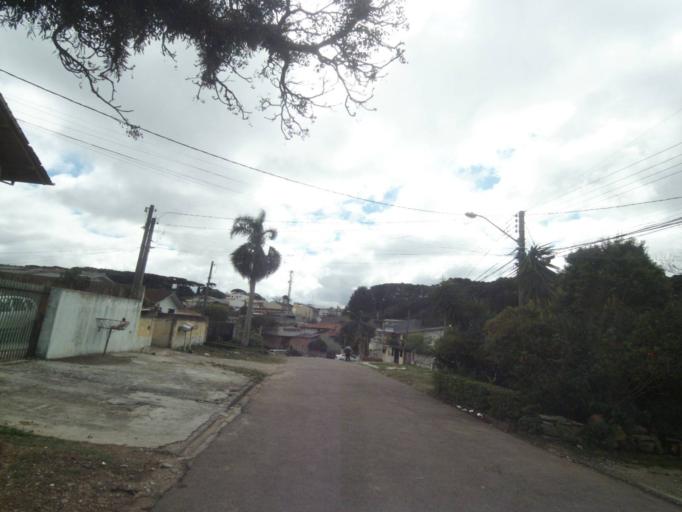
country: BR
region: Parana
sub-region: Sao Jose Dos Pinhais
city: Sao Jose dos Pinhais
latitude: -25.5382
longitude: -49.2889
